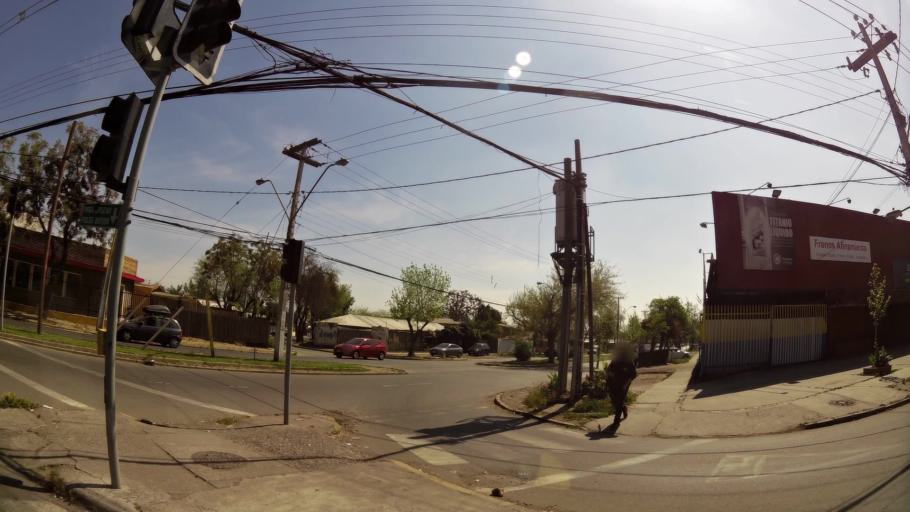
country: CL
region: Santiago Metropolitan
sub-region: Provincia de Santiago
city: Villa Presidente Frei, Nunoa, Santiago, Chile
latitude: -33.4790
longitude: -70.5831
